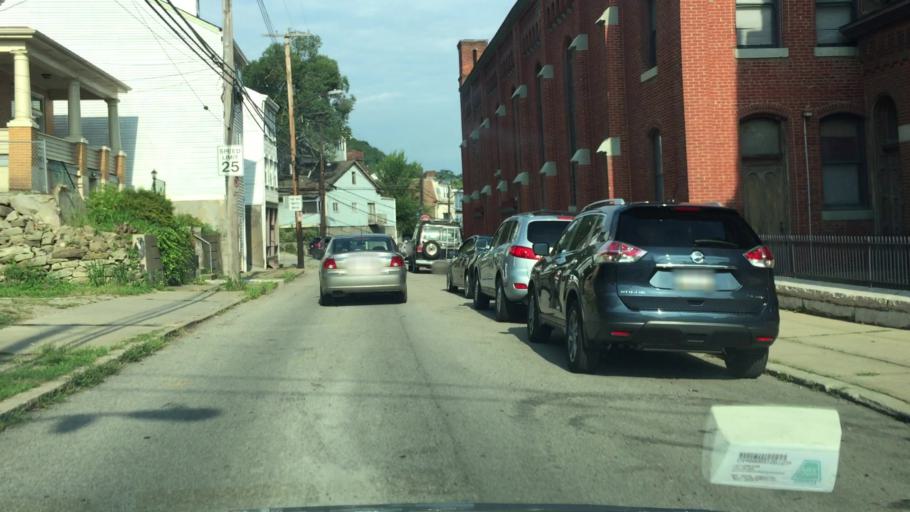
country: US
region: Pennsylvania
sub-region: Allegheny County
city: Mount Oliver
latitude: 40.4247
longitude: -79.9839
